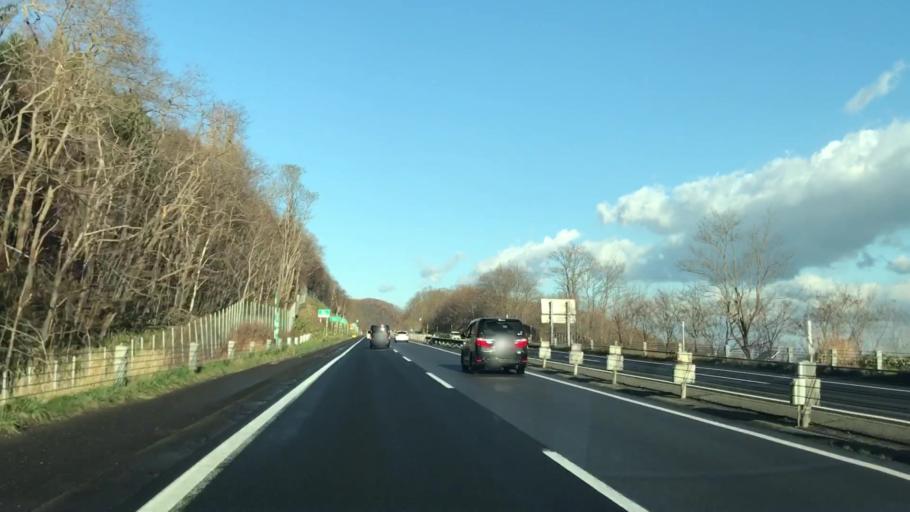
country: JP
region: Hokkaido
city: Sapporo
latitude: 43.0971
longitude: 141.2512
